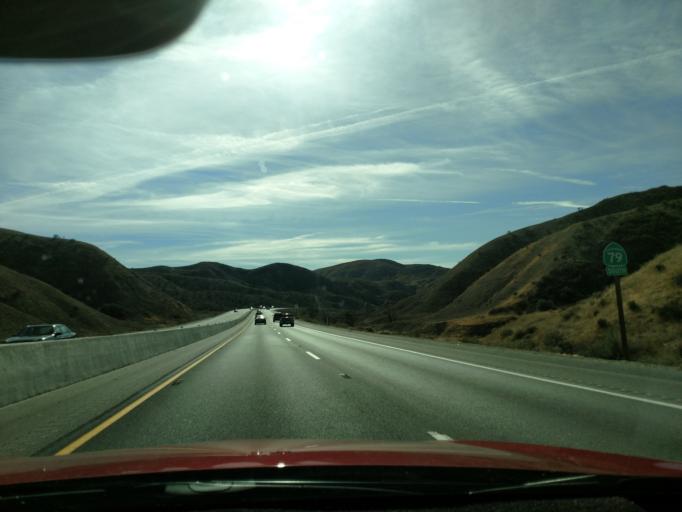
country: US
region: California
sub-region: Riverside County
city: Beaumont
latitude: 33.8796
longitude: -116.9913
